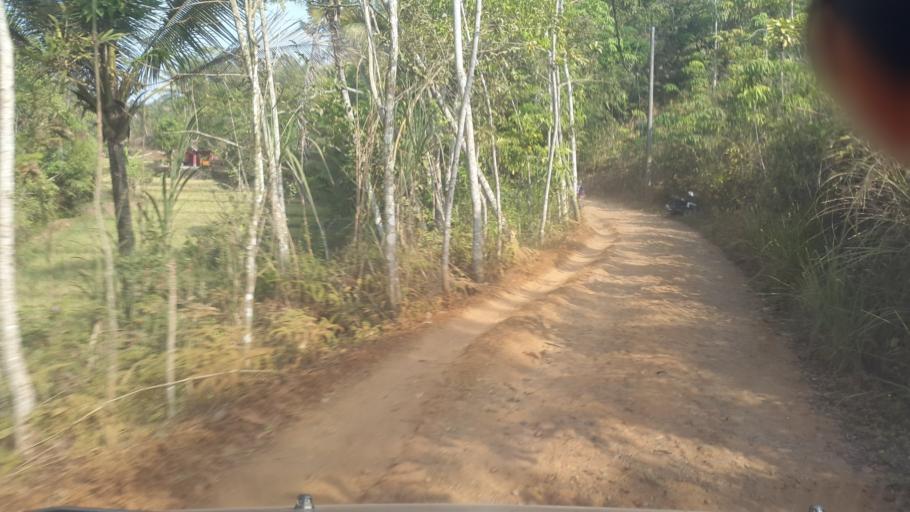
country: ID
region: West Java
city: Ciroyom
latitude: -7.1163
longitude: 106.8379
